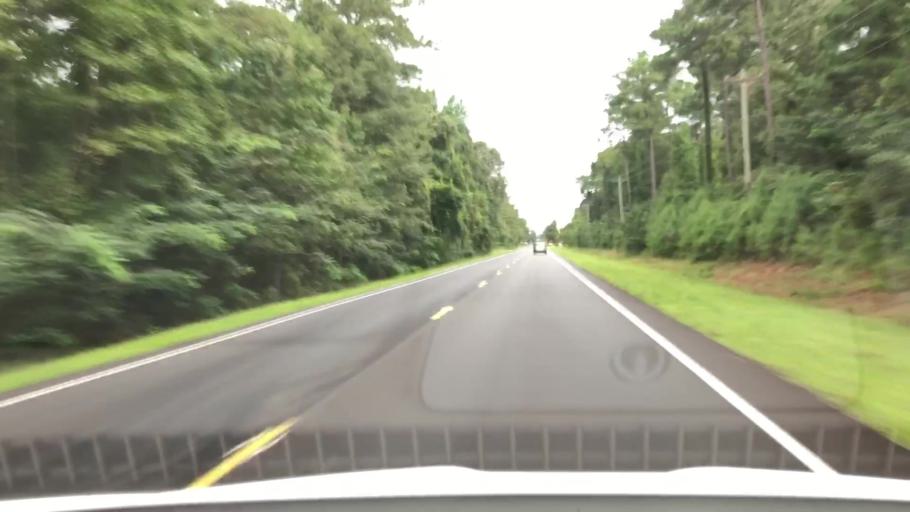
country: US
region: North Carolina
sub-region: Jones County
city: Maysville
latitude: 34.8752
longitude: -77.2003
